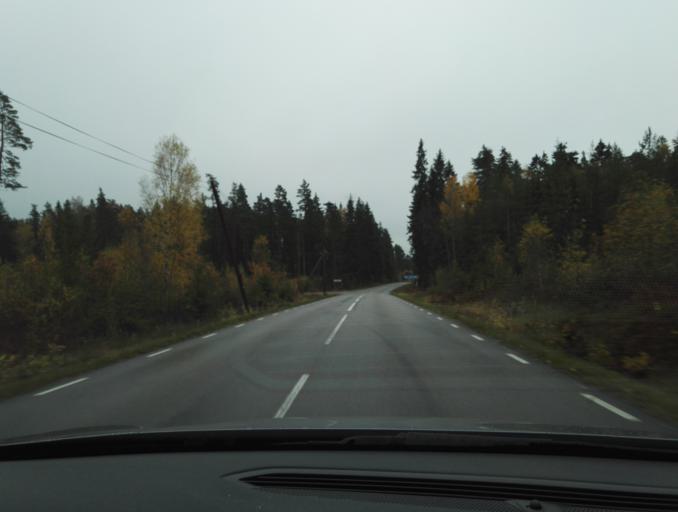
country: SE
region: Kronoberg
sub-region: Vaxjo Kommun
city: Rottne
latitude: 57.0247
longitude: 14.8303
